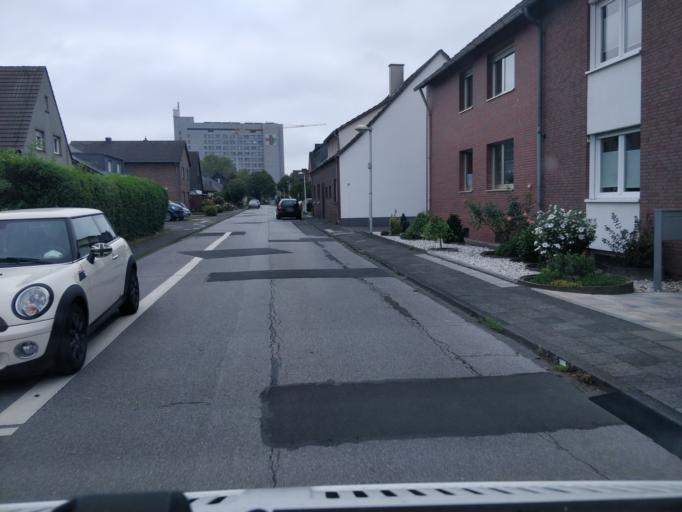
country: DE
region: North Rhine-Westphalia
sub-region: Regierungsbezirk Koln
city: Frechen
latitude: 50.9257
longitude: 6.8081
